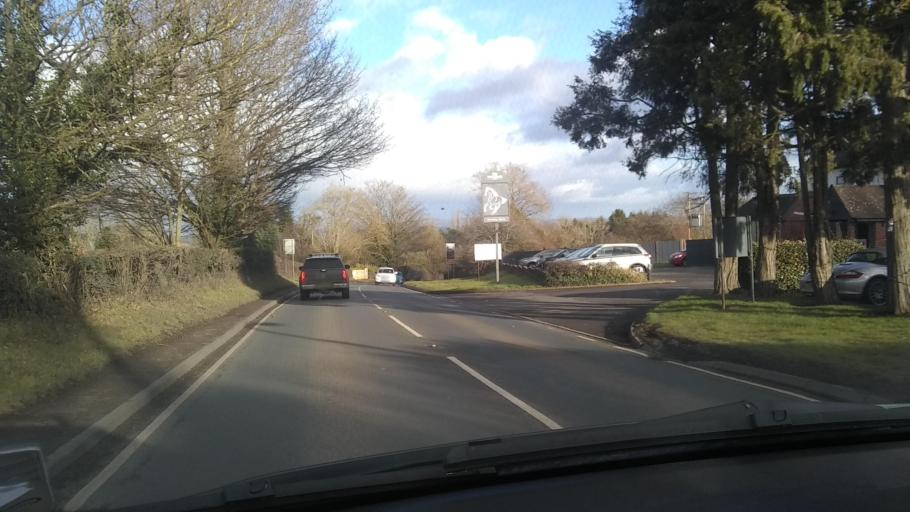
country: GB
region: England
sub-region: Worcestershire
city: Bewdley
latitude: 52.3684
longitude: -2.3478
